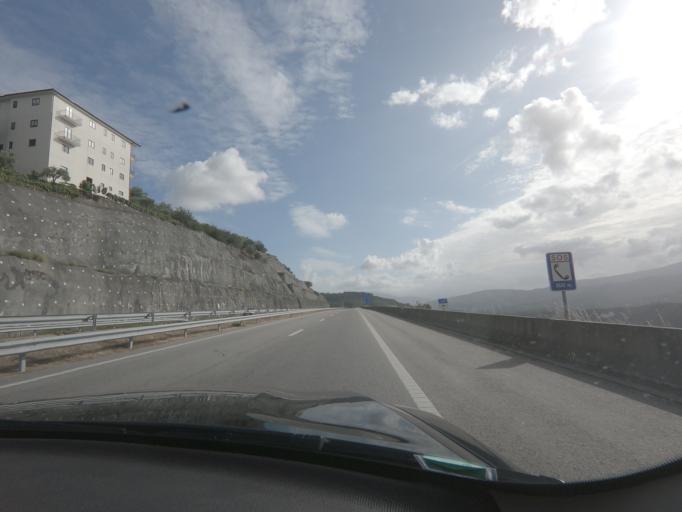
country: PT
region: Vila Real
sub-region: Vila Real
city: Vila Real
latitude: 41.2334
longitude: -7.7313
